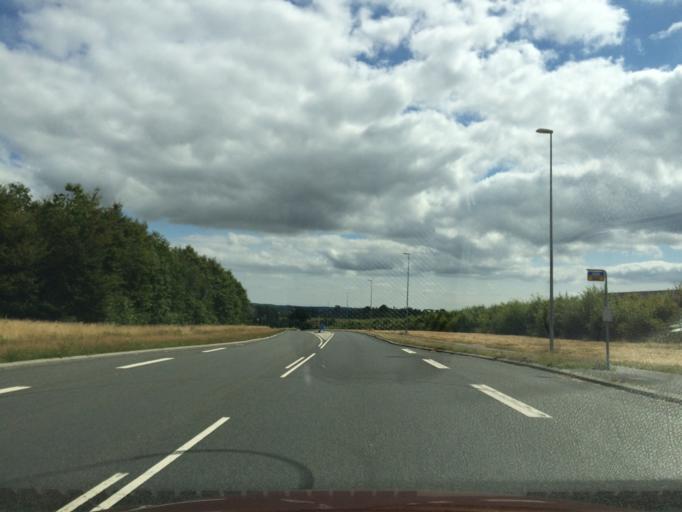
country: DK
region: Central Jutland
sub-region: Silkeborg Kommune
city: Svejbaek
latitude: 56.1893
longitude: 9.6128
